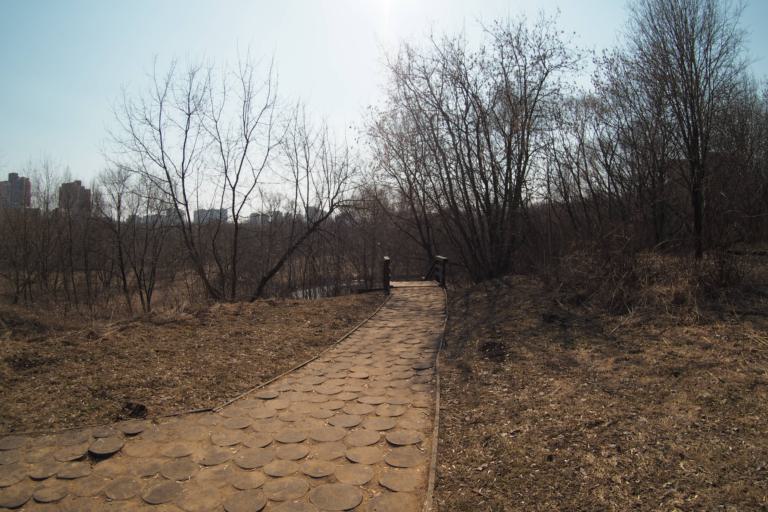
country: RU
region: Moscow
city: Davydkovo
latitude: 55.7158
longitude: 37.4666
